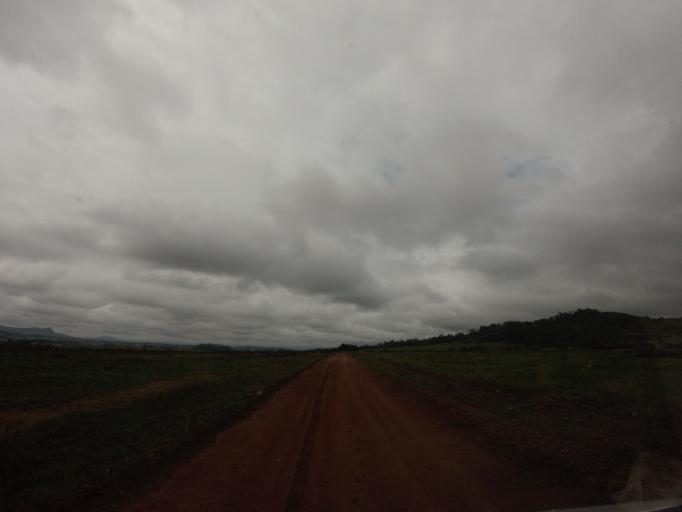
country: SZ
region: Hhohho
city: Lobamba
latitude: -26.4638
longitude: 31.1874
